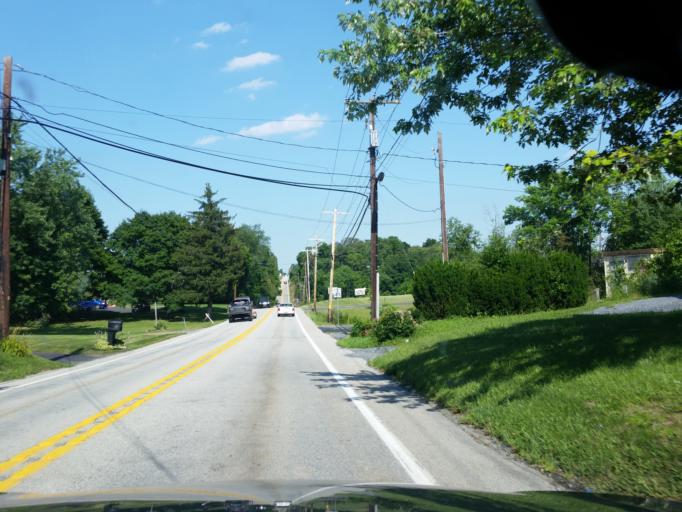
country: US
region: Pennsylvania
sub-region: Cumberland County
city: Mechanicsburg
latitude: 40.2846
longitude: -77.0343
